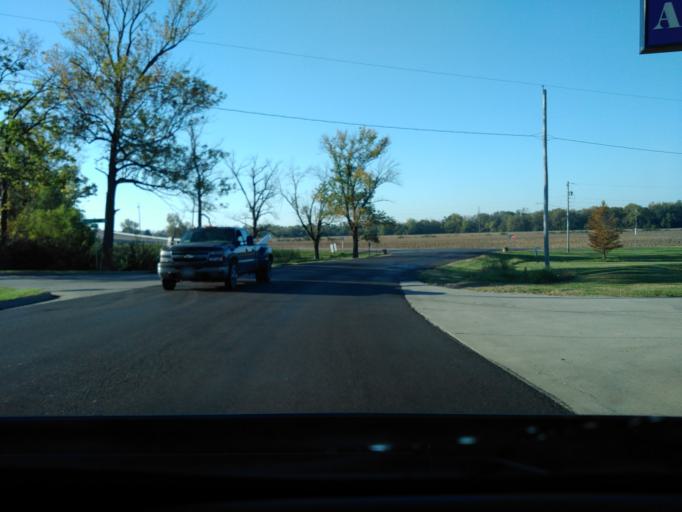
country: US
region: Illinois
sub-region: Bond County
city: Greenville
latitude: 38.8875
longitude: -89.3911
